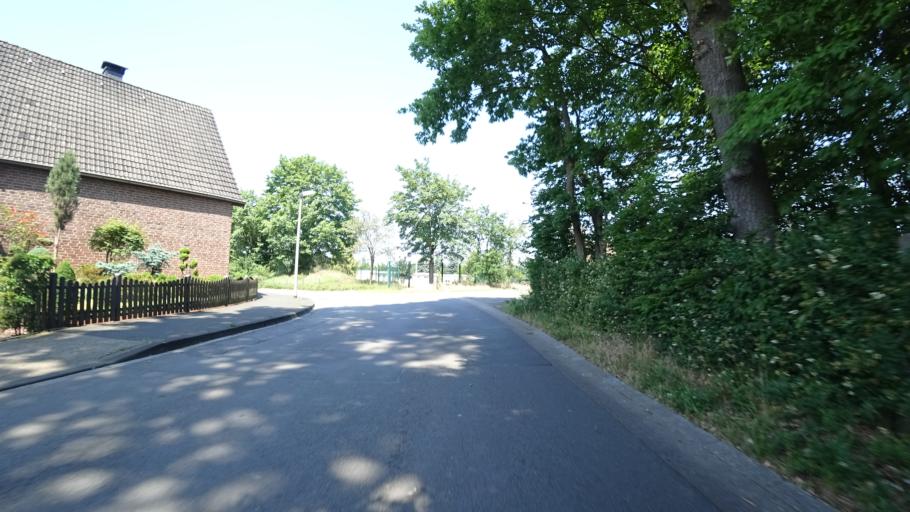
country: DE
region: North Rhine-Westphalia
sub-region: Regierungsbezirk Detmold
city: Guetersloh
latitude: 51.9342
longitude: 8.3681
